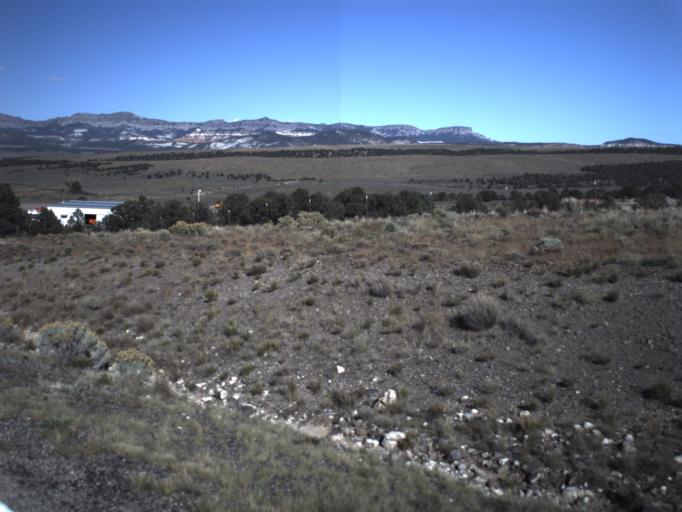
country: US
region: Utah
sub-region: Garfield County
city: Panguitch
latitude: 37.8006
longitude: -112.4366
